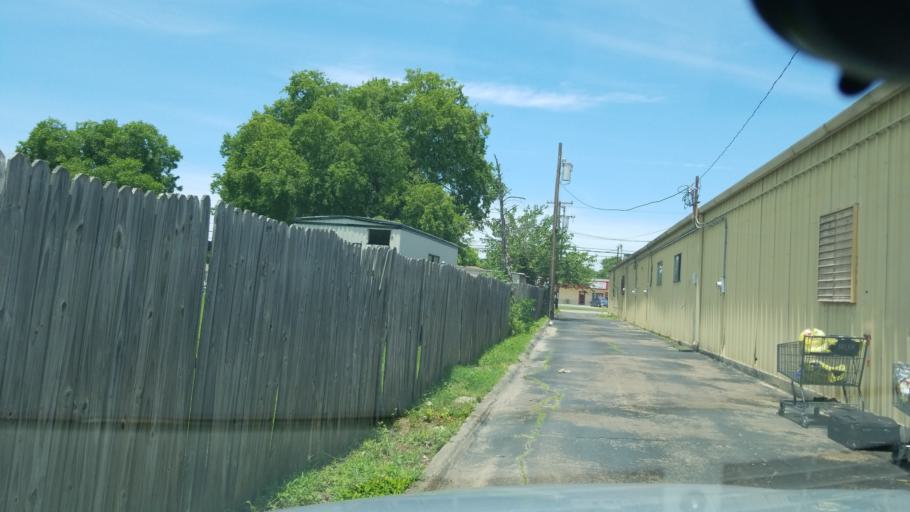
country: US
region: Texas
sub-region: Dallas County
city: Irving
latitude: 32.8168
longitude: -96.9335
